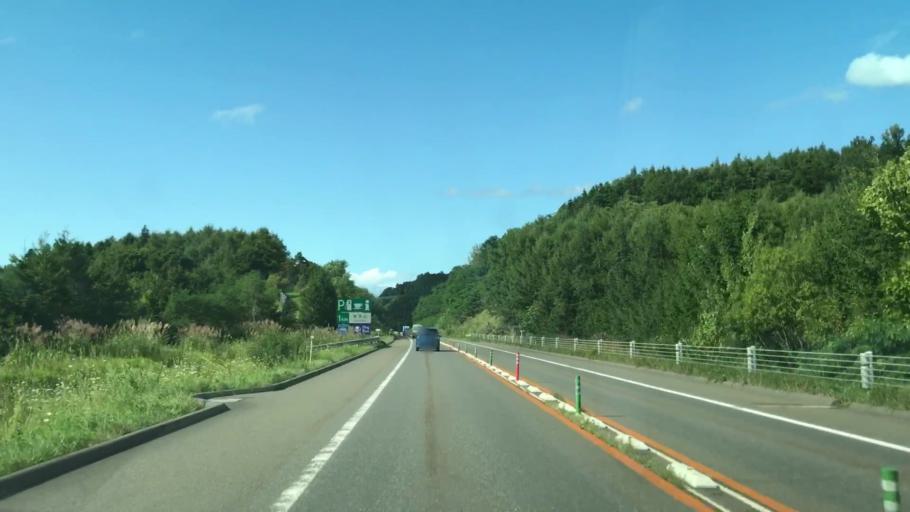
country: JP
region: Hokkaido
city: Date
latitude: 42.4542
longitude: 140.9130
